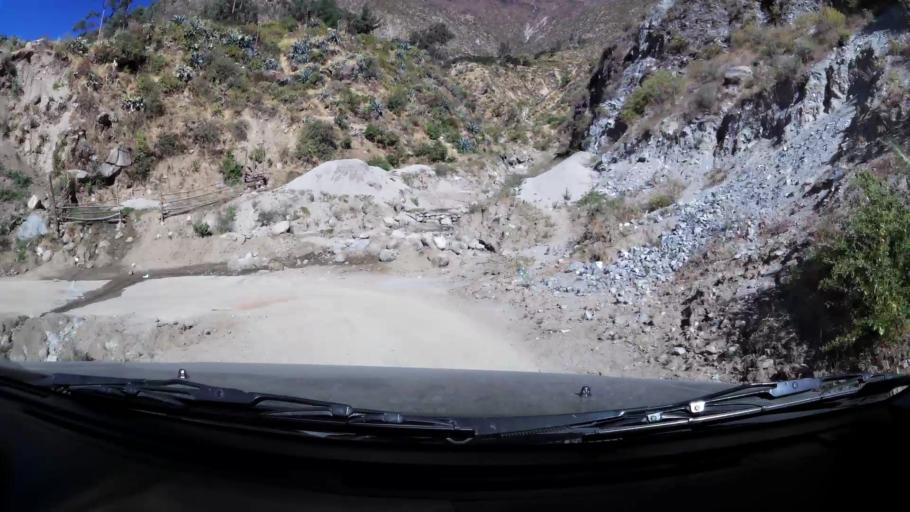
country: PE
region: Huancavelica
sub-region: Huaytara
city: Quito-Arma
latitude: -13.6096
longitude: -75.3487
